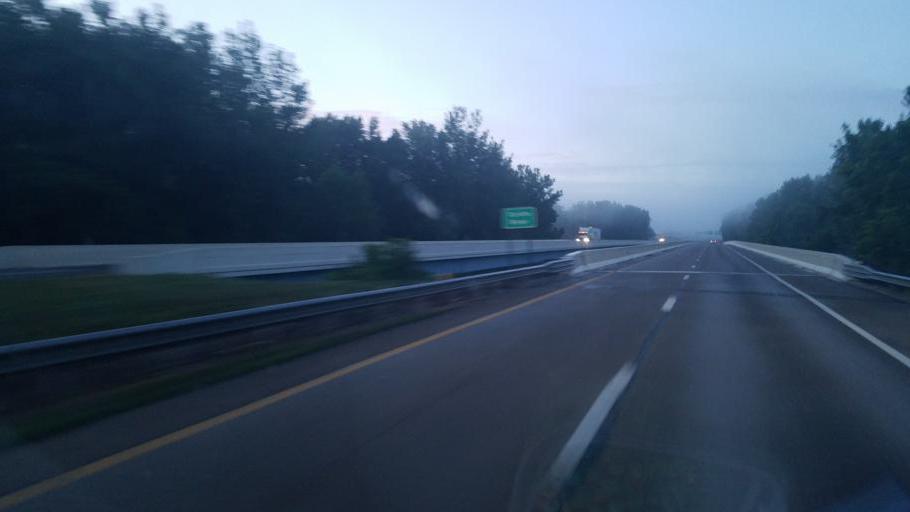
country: US
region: Ohio
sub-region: Ross County
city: Chillicothe
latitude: 39.3083
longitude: -82.9230
